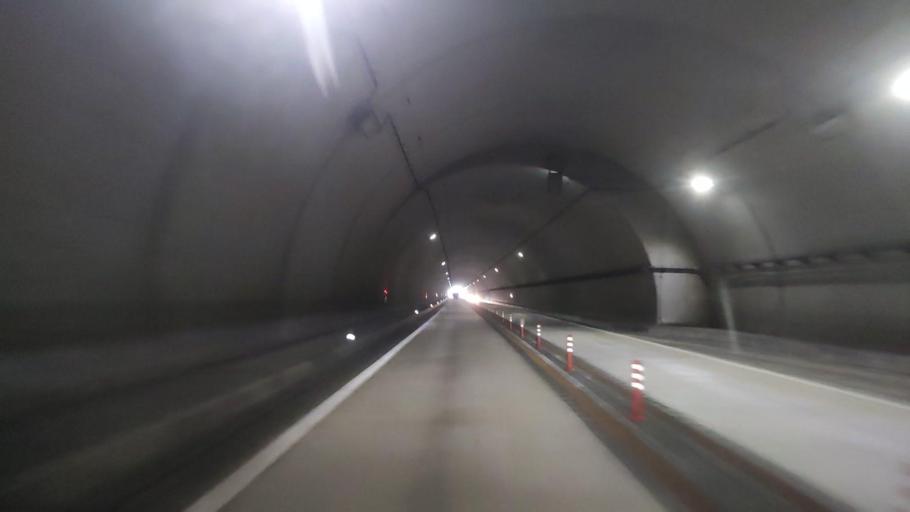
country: JP
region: Wakayama
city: Tanabe
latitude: 33.5640
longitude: 135.4992
